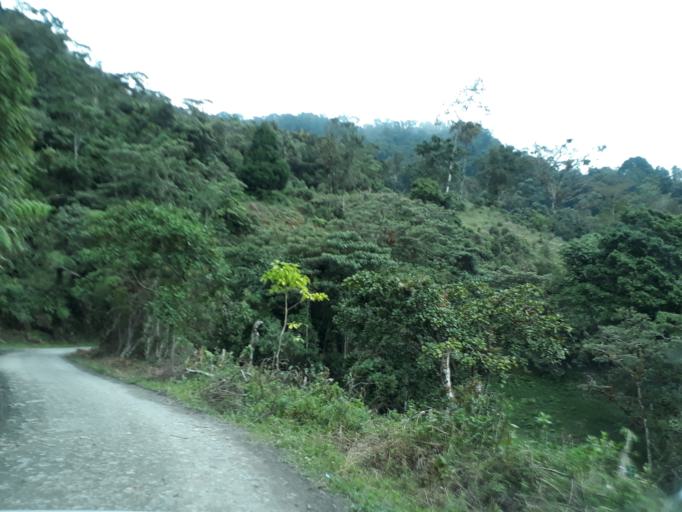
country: CO
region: Boyaca
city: Muzo
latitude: 5.3802
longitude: -74.0736
